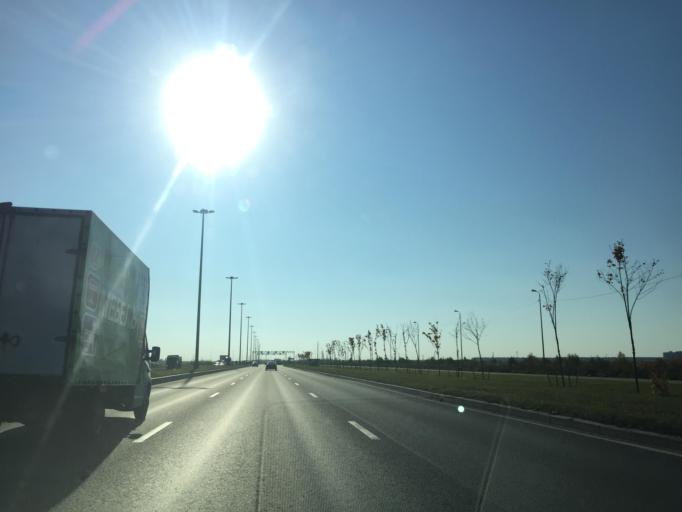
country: RU
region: St.-Petersburg
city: Petro-Slavyanka
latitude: 59.7752
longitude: 30.4988
